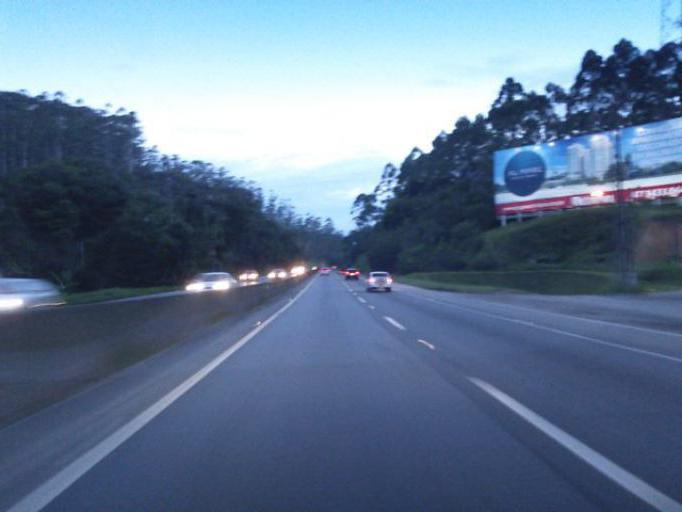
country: BR
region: Santa Catarina
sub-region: Joinville
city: Joinville
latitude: -26.4165
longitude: -48.8344
